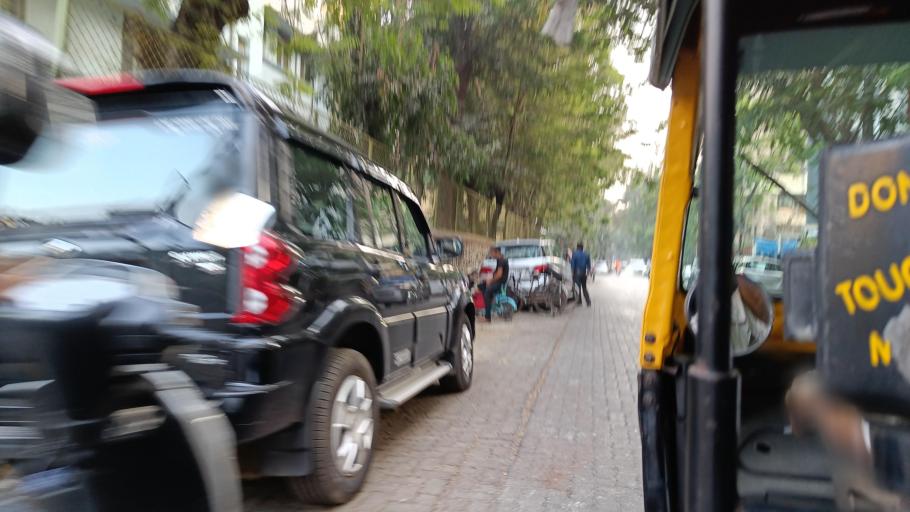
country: IN
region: Maharashtra
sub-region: Mumbai Suburban
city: Mumbai
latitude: 19.0629
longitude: 72.8329
